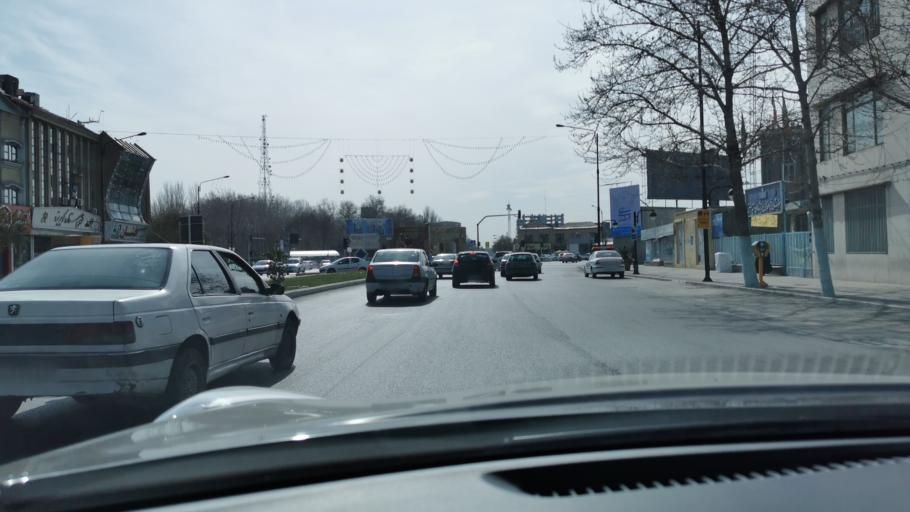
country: IR
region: Razavi Khorasan
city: Mashhad
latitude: 36.2919
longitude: 59.5851
